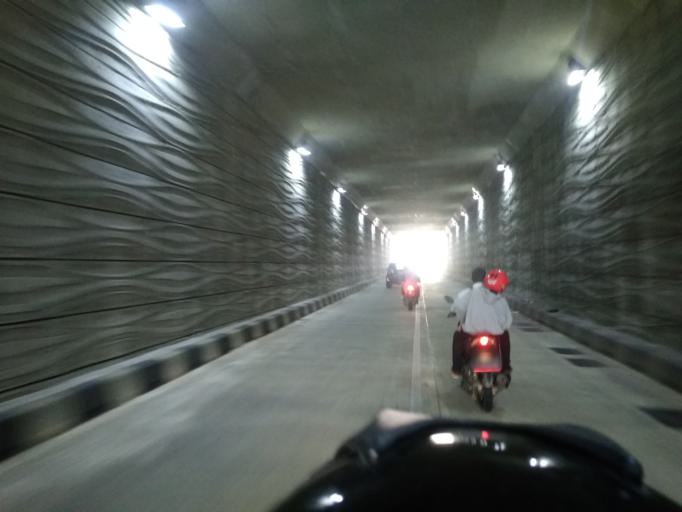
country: ID
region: Banten
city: South Tangerang
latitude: -6.2893
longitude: 106.7761
